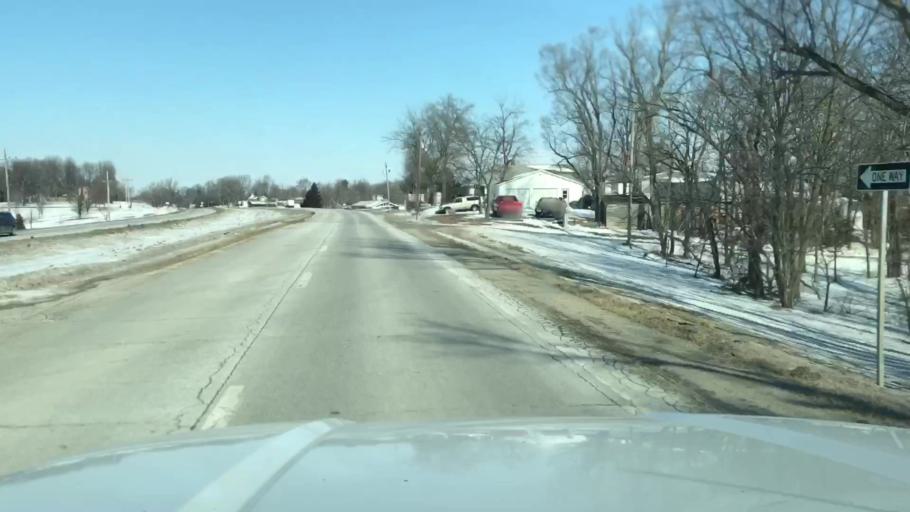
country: US
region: Missouri
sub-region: Andrew County
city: Savannah
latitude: 39.9089
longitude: -94.8091
